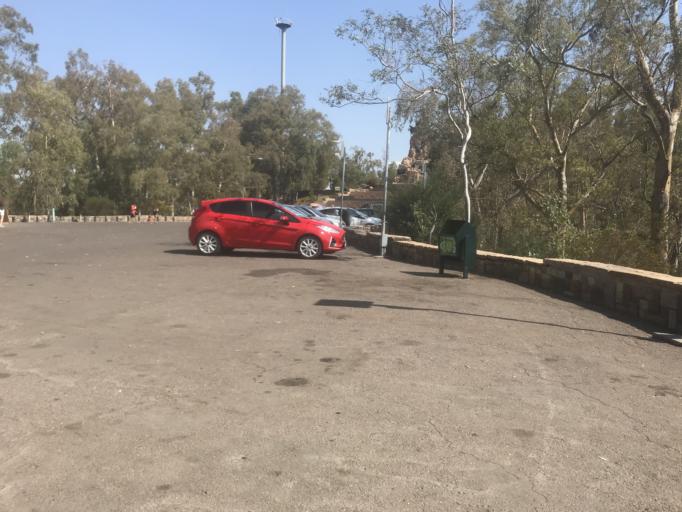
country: AR
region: Mendoza
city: Mendoza
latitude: -32.8875
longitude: -68.8912
